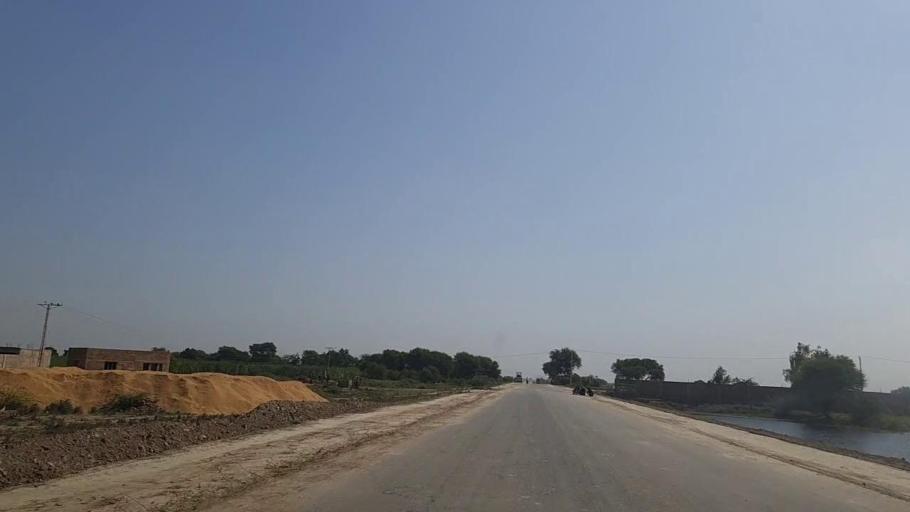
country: PK
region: Sindh
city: Daro Mehar
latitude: 24.7906
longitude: 68.1870
